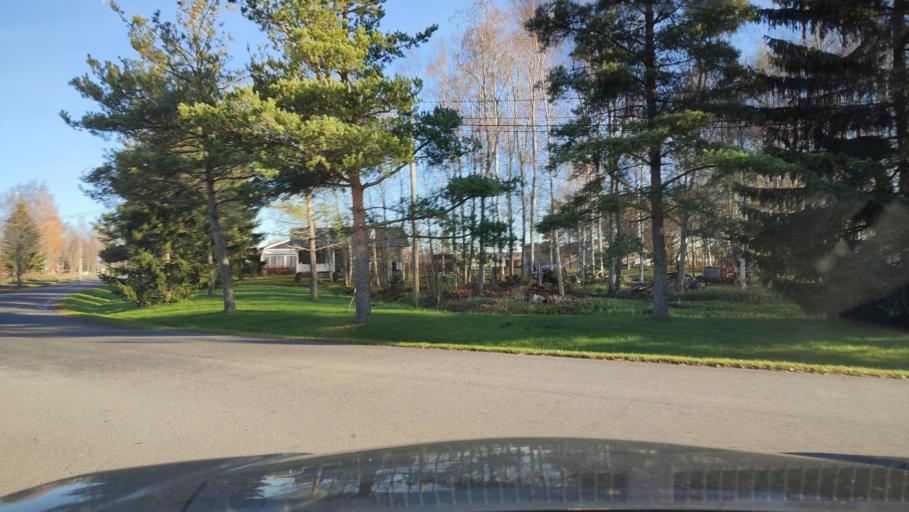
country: FI
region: Southern Ostrobothnia
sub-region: Suupohja
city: Teuva
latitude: 62.4739
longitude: 21.7480
